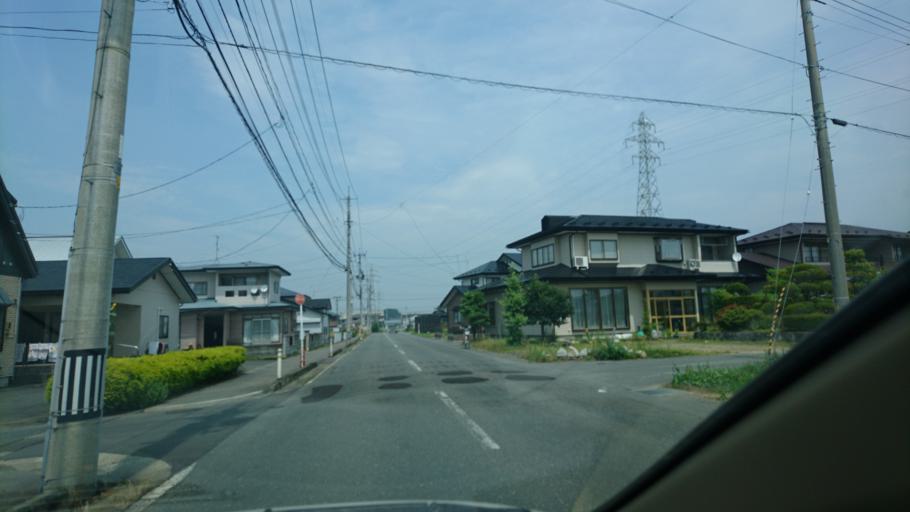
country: JP
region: Iwate
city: Kitakami
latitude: 39.2726
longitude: 141.0936
